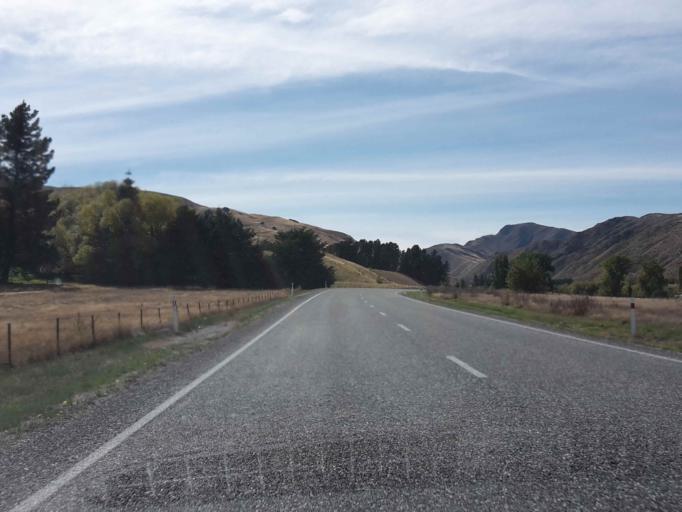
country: NZ
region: Otago
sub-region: Queenstown-Lakes District
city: Wanaka
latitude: -44.6480
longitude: 169.4978
